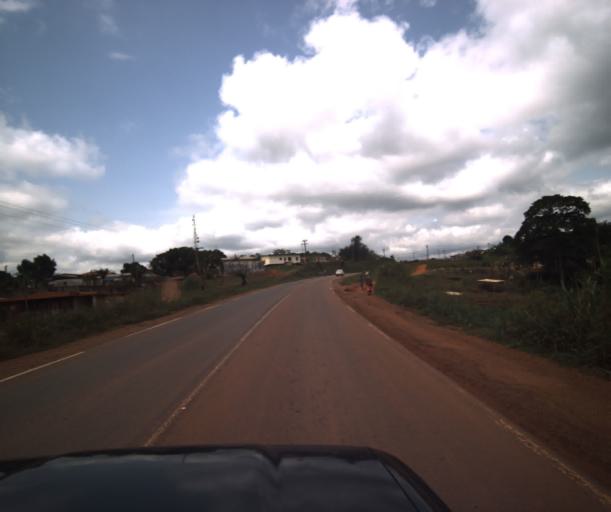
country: CM
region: Centre
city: Mbankomo
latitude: 3.7883
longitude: 11.4046
